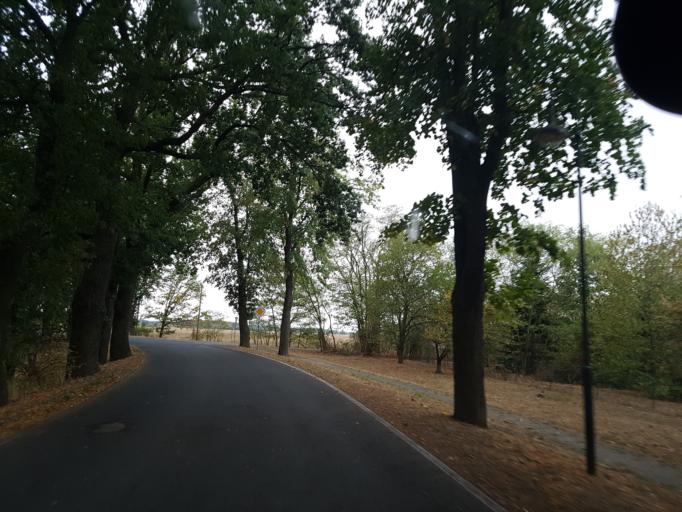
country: DE
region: Saxony-Anhalt
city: Annaburg
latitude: 51.7801
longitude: 13.0536
